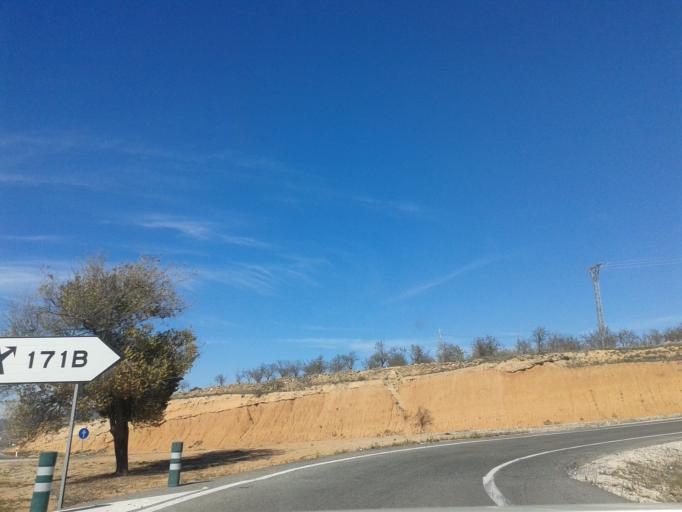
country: ES
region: Castille-La Mancha
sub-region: Provincia de Albacete
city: Caudete
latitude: 38.7328
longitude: -0.9403
